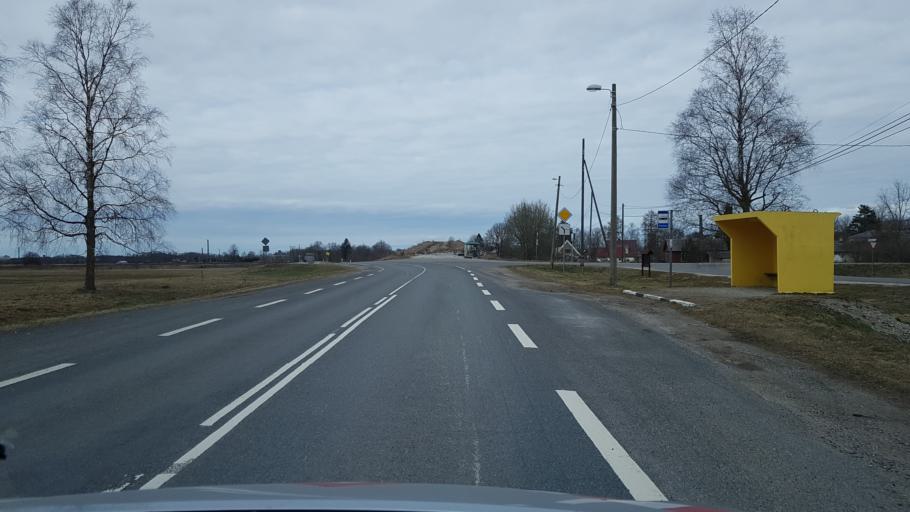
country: EE
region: Ida-Virumaa
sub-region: Sillamaee linn
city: Sillamae
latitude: 59.3706
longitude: 27.7610
